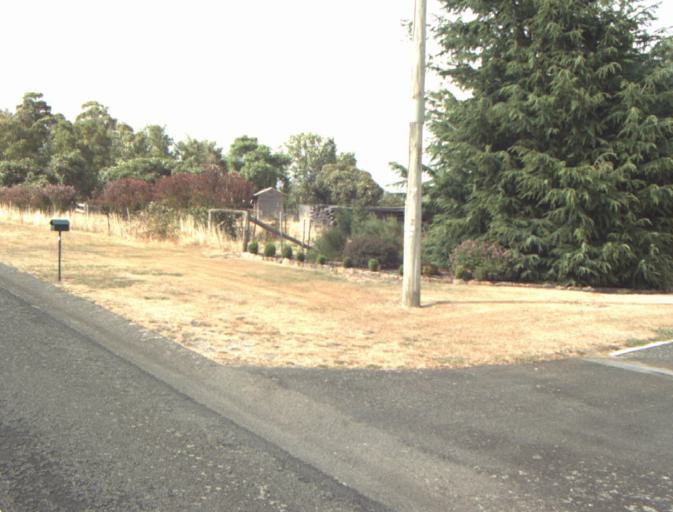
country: AU
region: Tasmania
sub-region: Launceston
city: Mayfield
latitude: -41.3273
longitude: 147.0575
